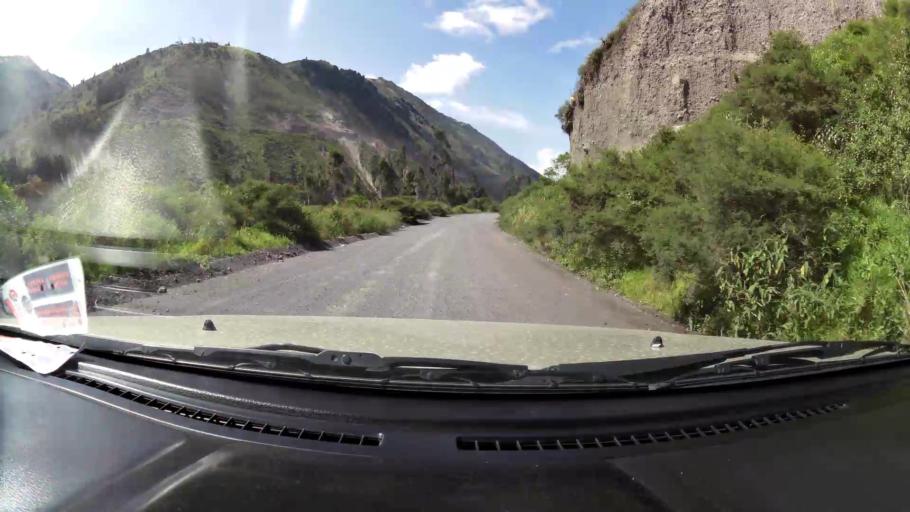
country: EC
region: Tungurahua
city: Banos
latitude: -1.4951
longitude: -78.5127
